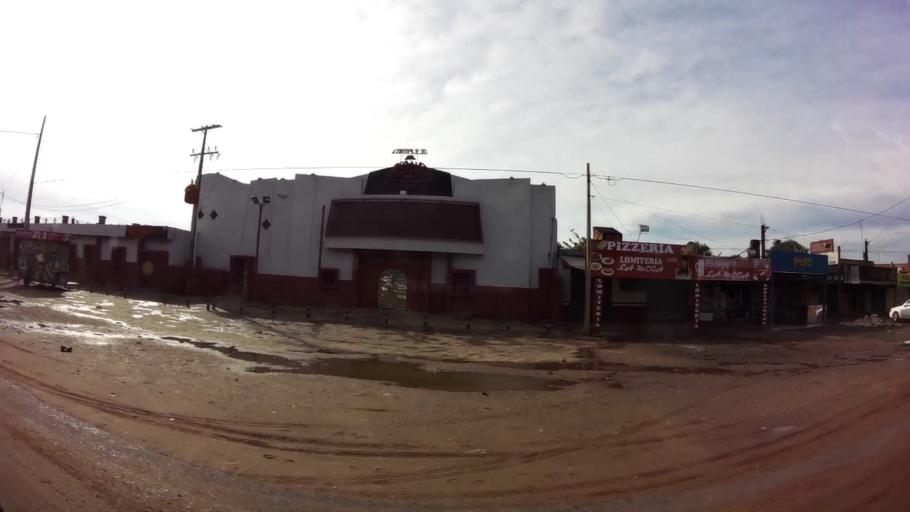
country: PY
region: Central
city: Limpio
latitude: -25.1724
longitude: -57.4817
